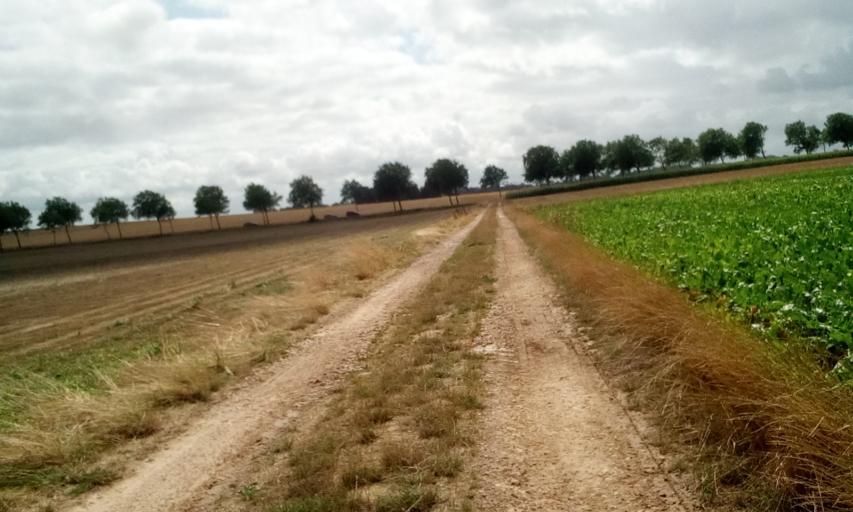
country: FR
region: Lower Normandy
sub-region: Departement du Calvados
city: Cheux
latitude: 49.1758
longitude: -0.5432
